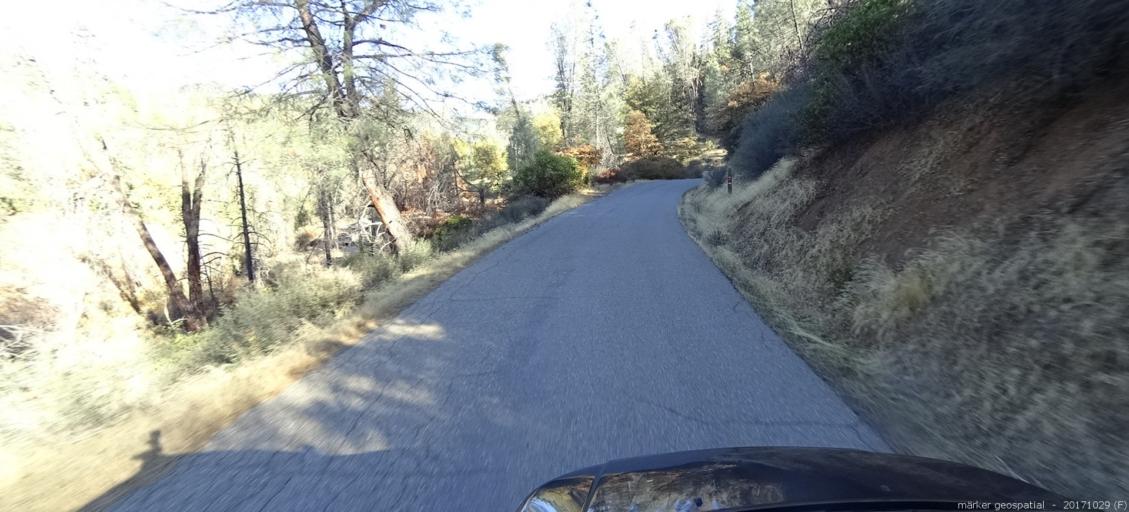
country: US
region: California
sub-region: Trinity County
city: Hayfork
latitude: 40.3735
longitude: -122.9762
